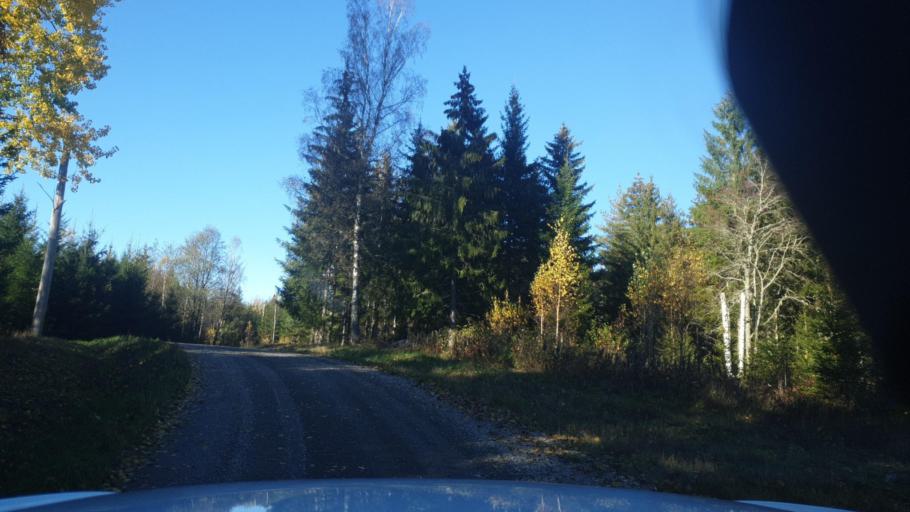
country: SE
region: Vaermland
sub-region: Arvika Kommun
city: Arvika
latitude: 59.5569
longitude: 12.8473
